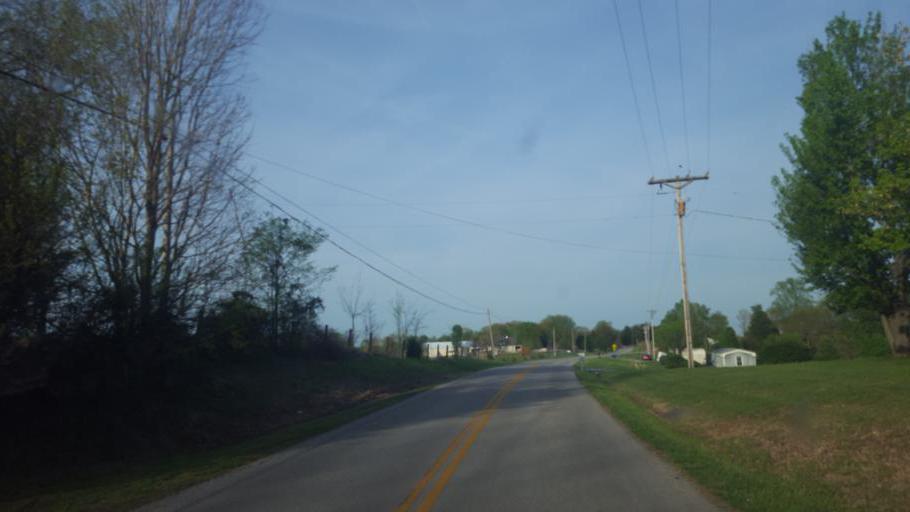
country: US
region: Kentucky
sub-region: Allen County
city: Scottsville
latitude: 36.9166
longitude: -86.1031
